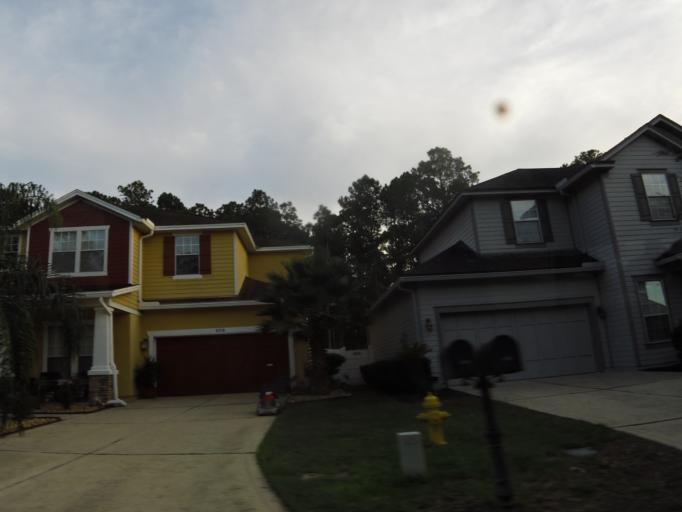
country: US
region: Florida
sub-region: Saint Johns County
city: Fruit Cove
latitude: 30.1536
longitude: -81.5450
